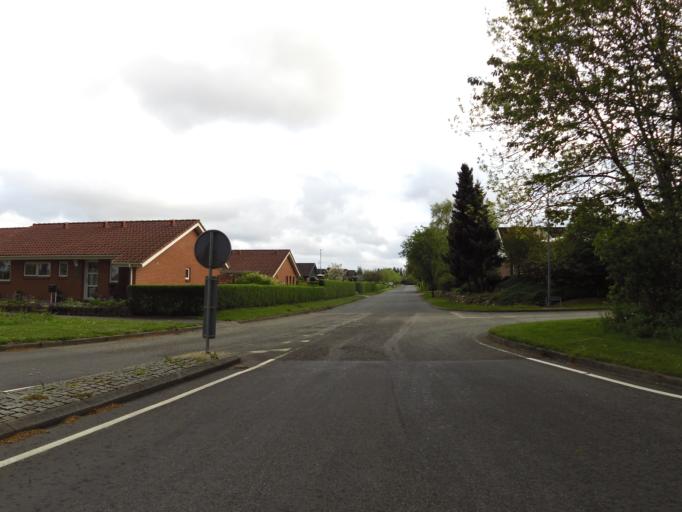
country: DK
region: South Denmark
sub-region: Haderslev Kommune
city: Gram
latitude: 55.2901
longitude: 9.0404
